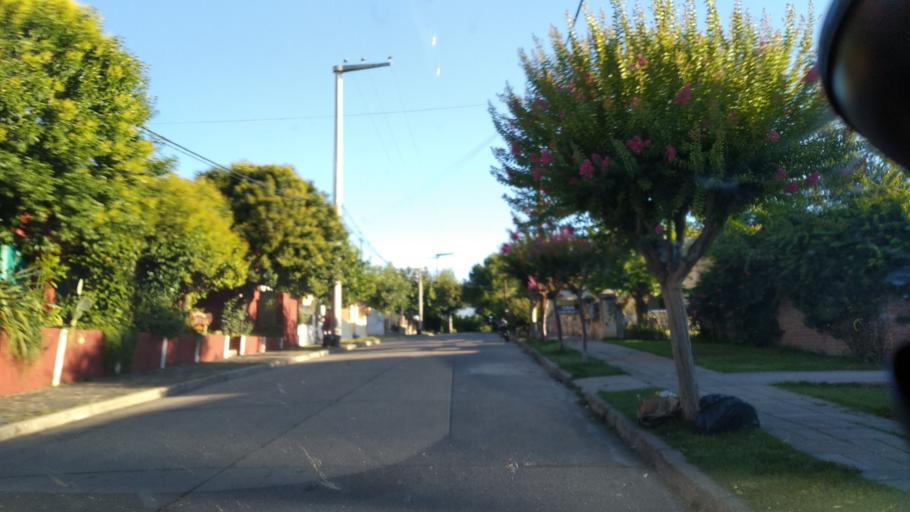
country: AR
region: Cordoba
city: Mina Clavero
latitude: -31.7166
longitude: -65.0035
